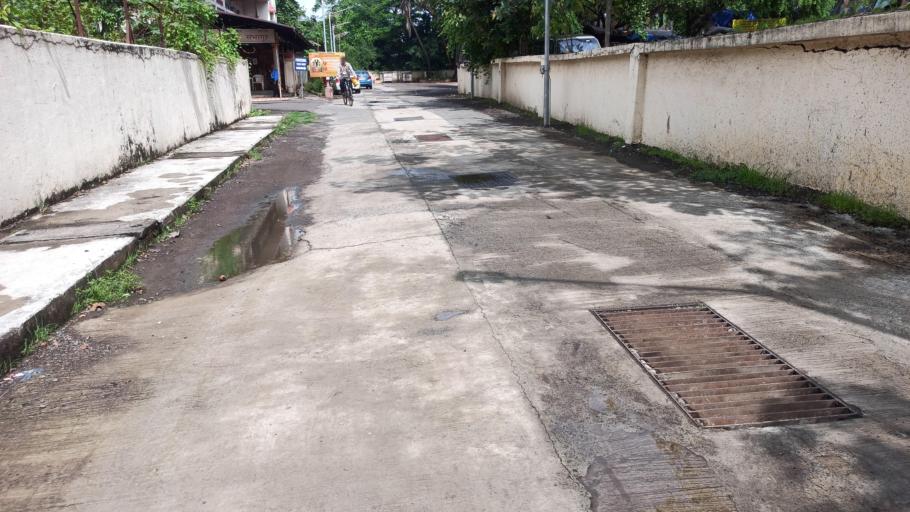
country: IN
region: Maharashtra
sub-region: Mumbai Suburban
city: Borivli
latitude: 19.2614
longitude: 72.8603
